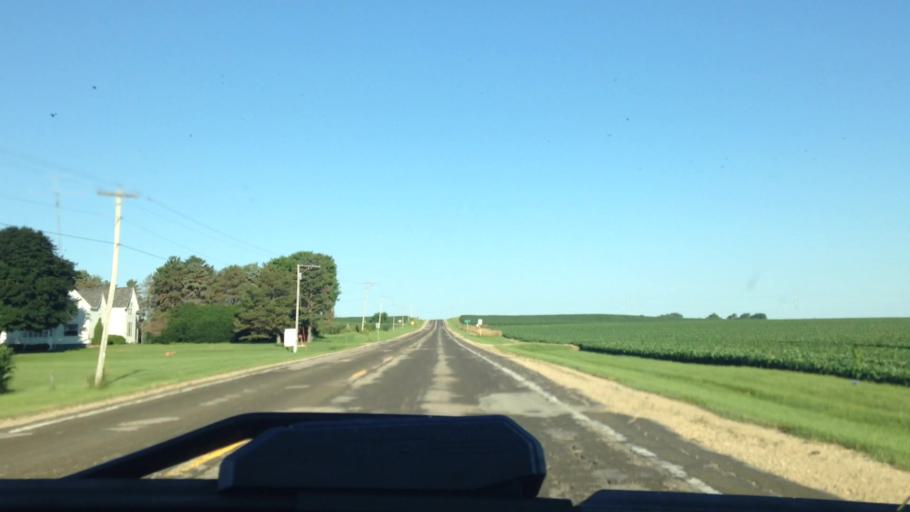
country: US
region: Wisconsin
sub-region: Columbia County
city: Poynette
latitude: 43.3377
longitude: -89.3881
